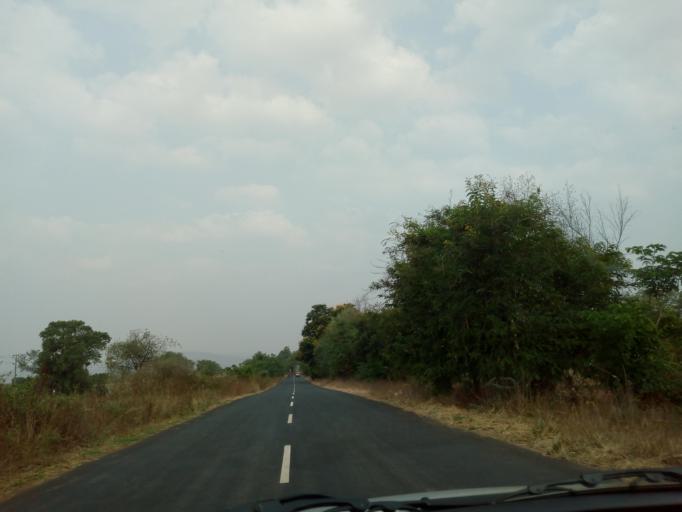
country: IN
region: Andhra Pradesh
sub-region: Prakasam
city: Diguvametta
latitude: 15.3781
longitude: 78.8599
